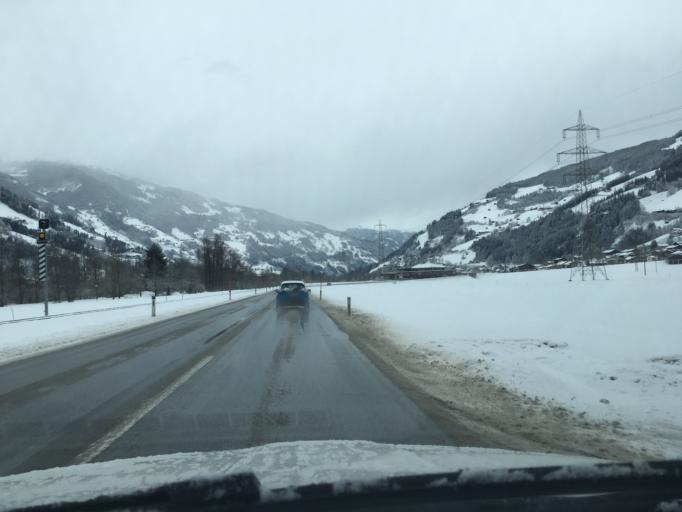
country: AT
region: Tyrol
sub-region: Politischer Bezirk Schwaz
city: Schwendau
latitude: 47.1860
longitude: 11.8664
